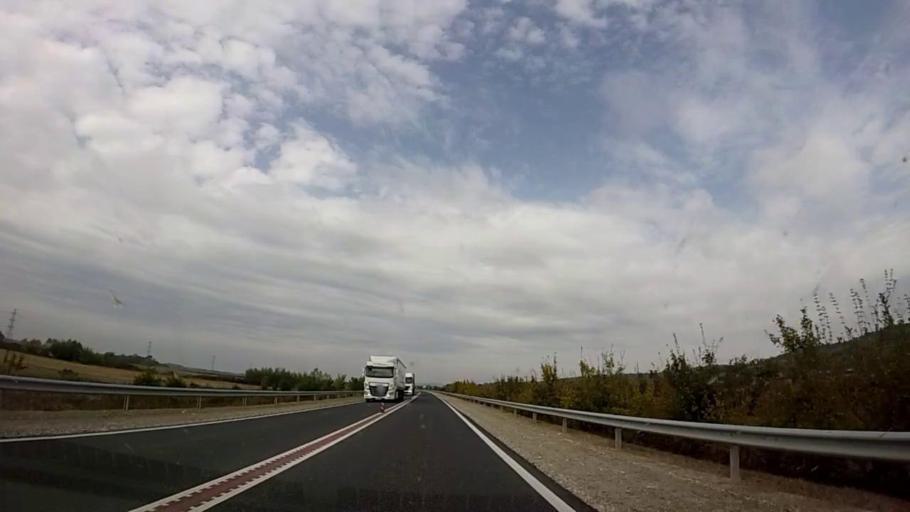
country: HR
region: Medimurska
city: Domasinec
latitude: 46.4970
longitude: 16.6249
